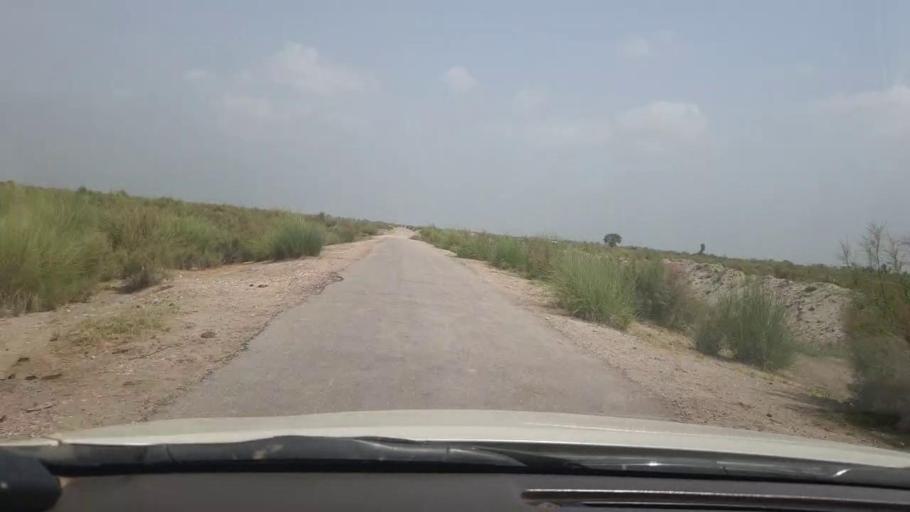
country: PK
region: Sindh
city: Garhi Yasin
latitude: 28.0168
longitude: 68.4999
